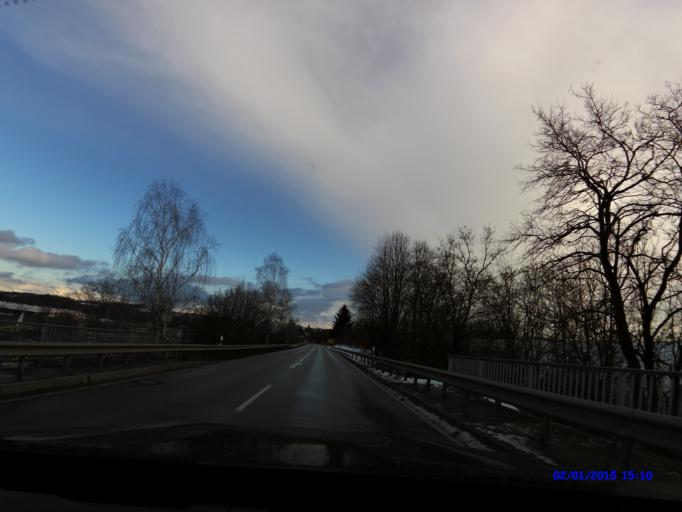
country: DE
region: Bavaria
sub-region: Lower Bavaria
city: Mainburg
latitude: 48.6306
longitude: 11.7719
